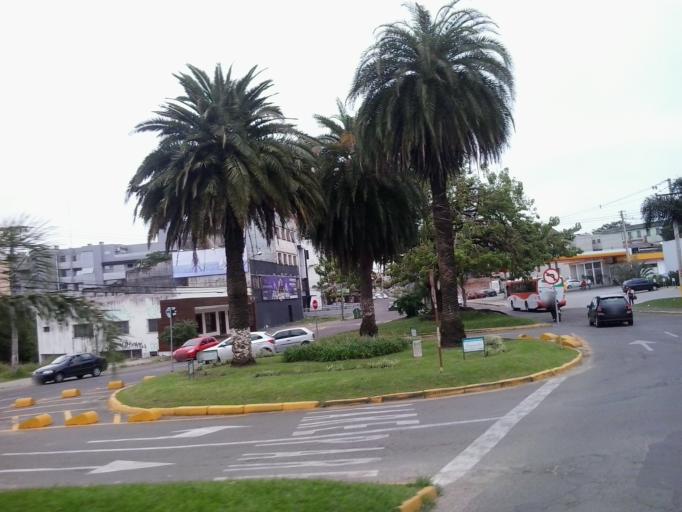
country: BR
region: Rio Grande do Sul
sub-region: Santa Maria
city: Santa Maria
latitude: -29.6896
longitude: -53.7922
